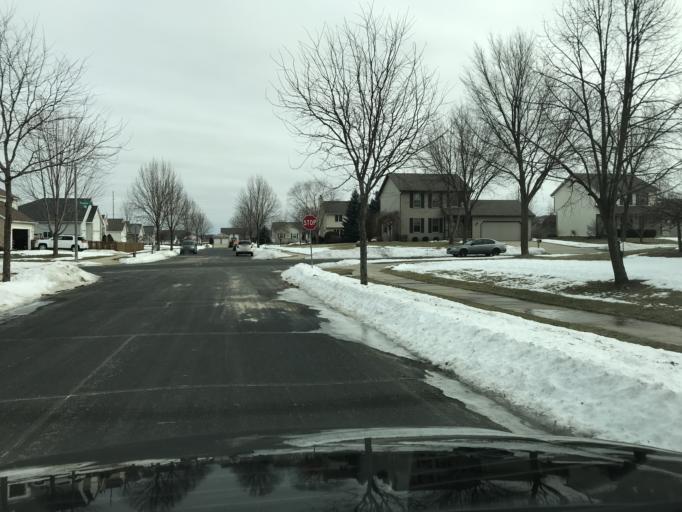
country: US
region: Wisconsin
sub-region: Dane County
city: Monona
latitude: 43.0908
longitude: -89.2705
